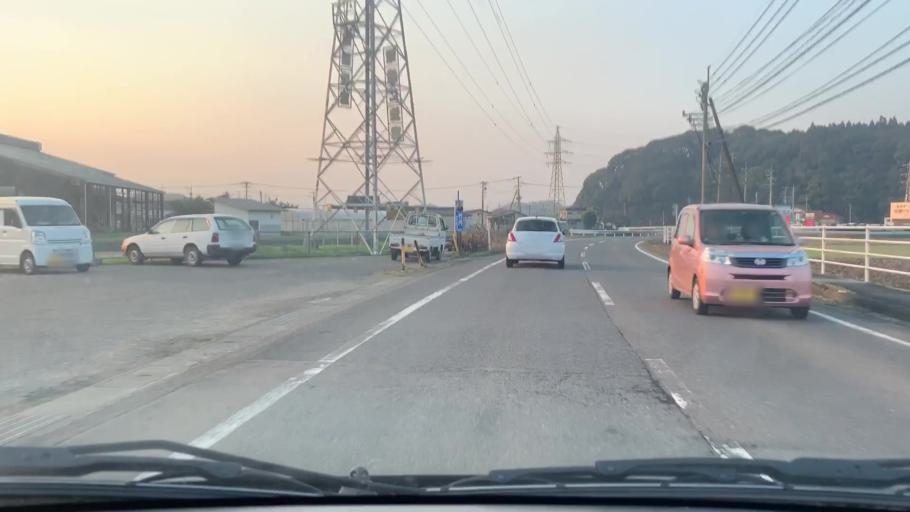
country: JP
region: Saga Prefecture
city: Imaricho-ko
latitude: 33.2697
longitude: 129.8962
